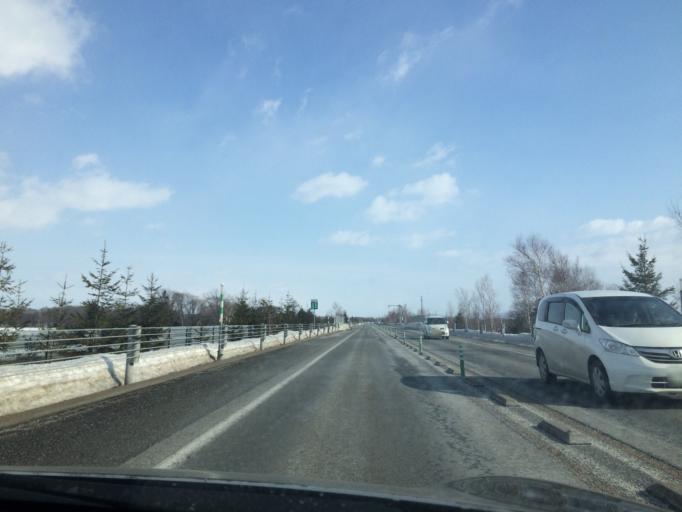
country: JP
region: Hokkaido
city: Chitose
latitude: 42.8718
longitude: 141.6138
